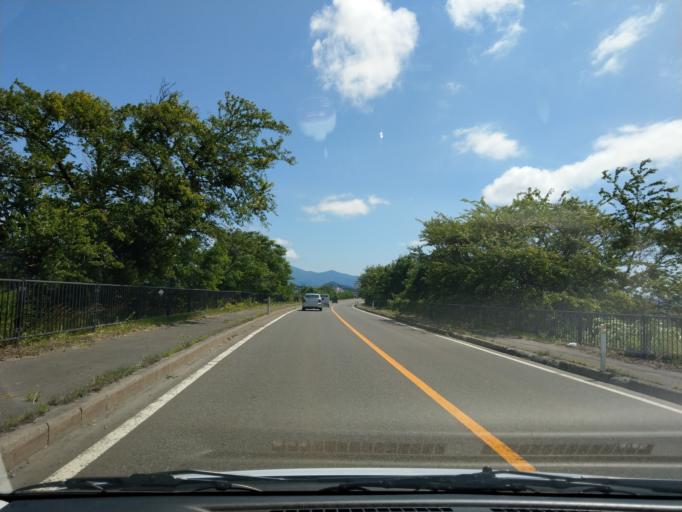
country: JP
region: Akita
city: Odate
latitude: 40.2900
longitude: 140.5639
